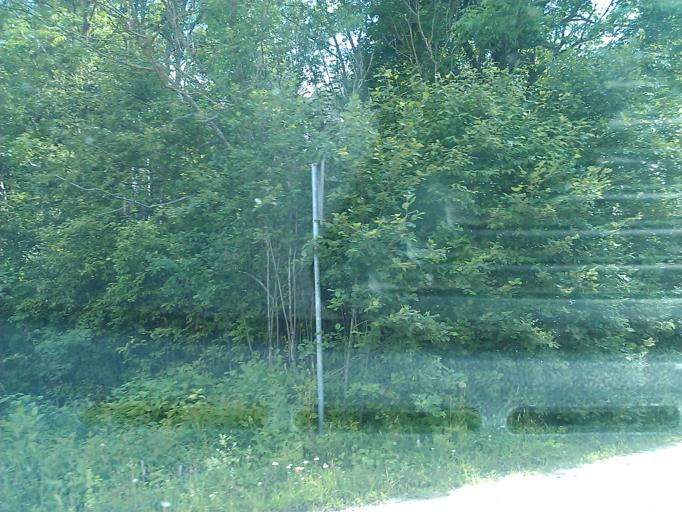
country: LV
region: Priekuli
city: Priekuli
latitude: 57.3345
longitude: 25.3259
